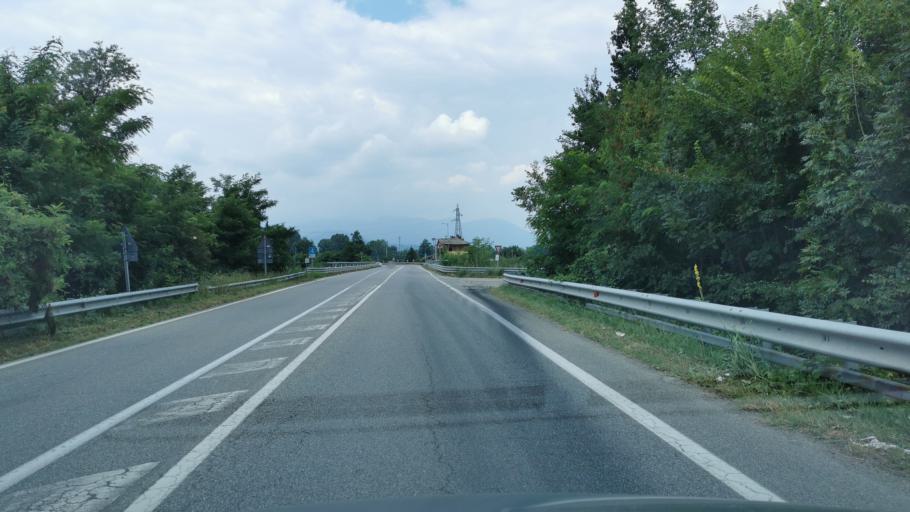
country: IT
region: Piedmont
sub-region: Provincia di Torino
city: Garzigliana
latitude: 44.8280
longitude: 7.3684
